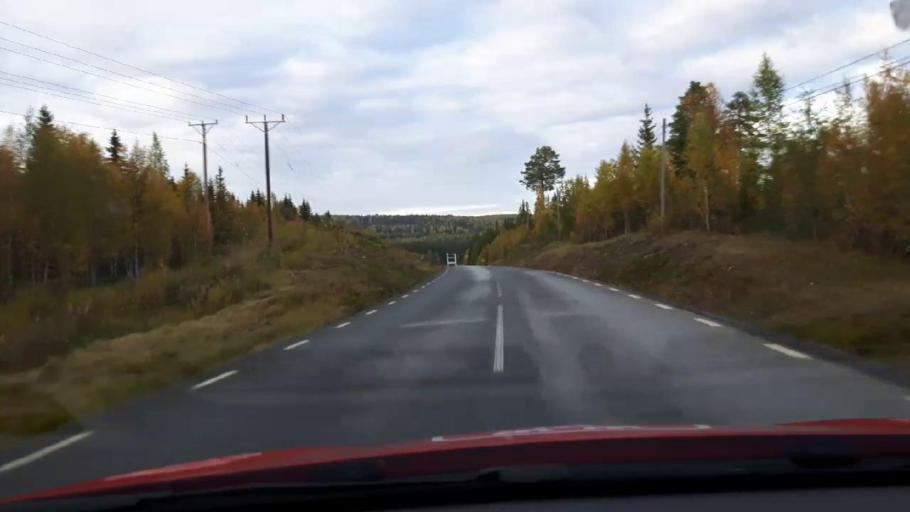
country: SE
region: Jaemtland
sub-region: OEstersunds Kommun
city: Lit
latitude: 63.3157
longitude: 14.7190
